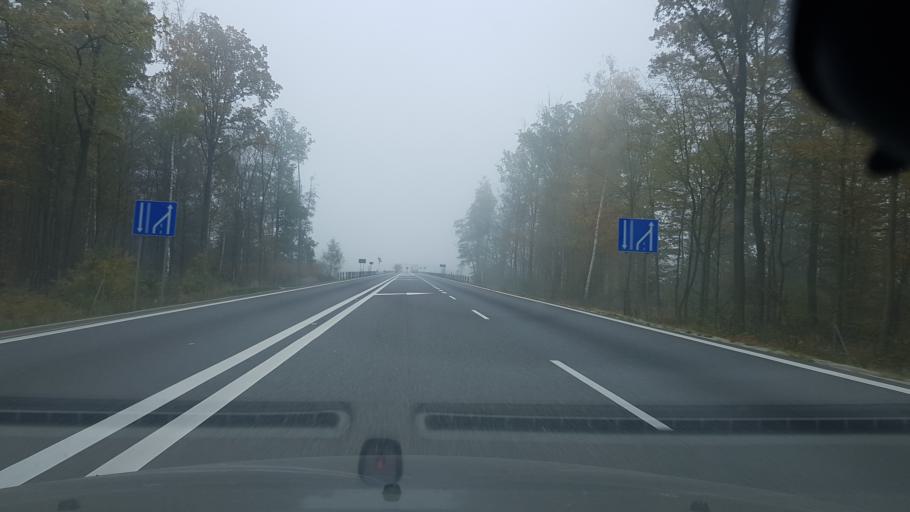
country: PL
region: Masovian Voivodeship
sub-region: Powiat zyrardowski
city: Zyrardow
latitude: 52.0296
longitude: 20.4336
